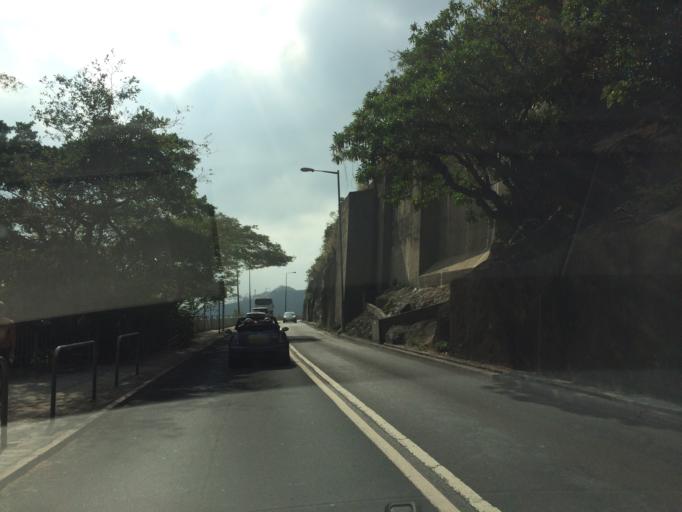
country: HK
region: Wanchai
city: Wan Chai
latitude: 22.2461
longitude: 114.1857
